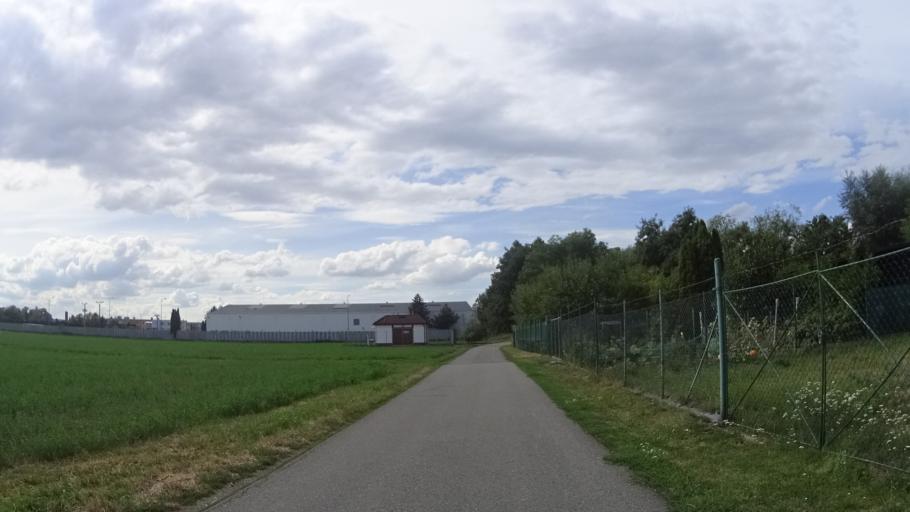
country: CZ
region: Olomoucky
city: Litovel
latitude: 49.6986
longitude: 17.0881
